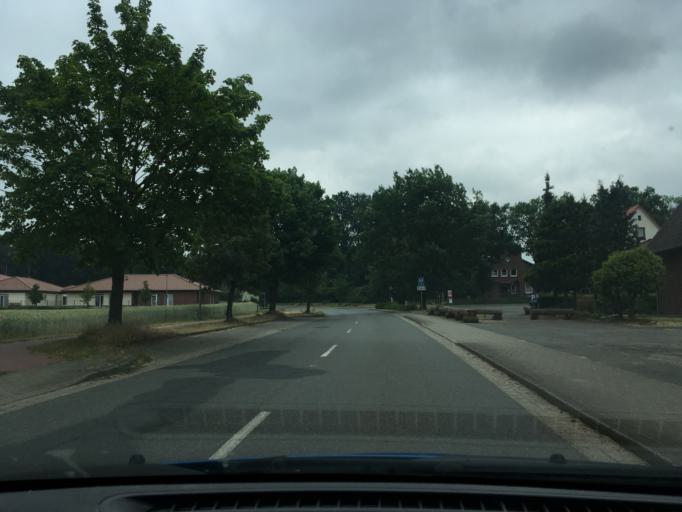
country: DE
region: Lower Saxony
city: Zernien
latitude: 53.0678
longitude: 10.8853
